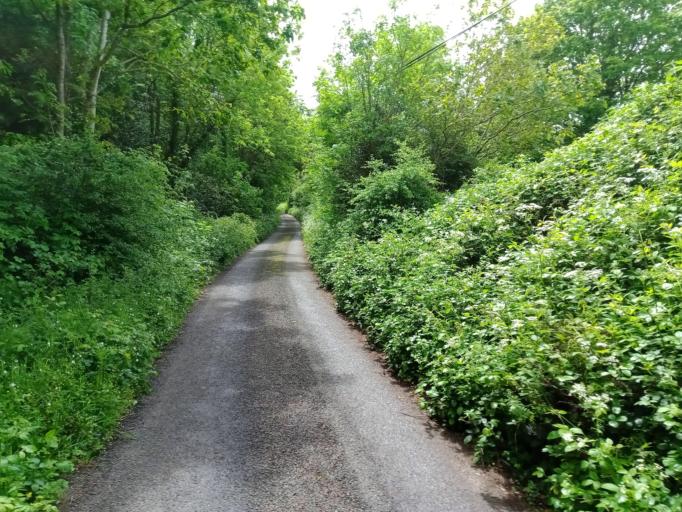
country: IE
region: Leinster
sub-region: Kilkenny
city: Thomastown
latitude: 52.5091
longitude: -7.1309
